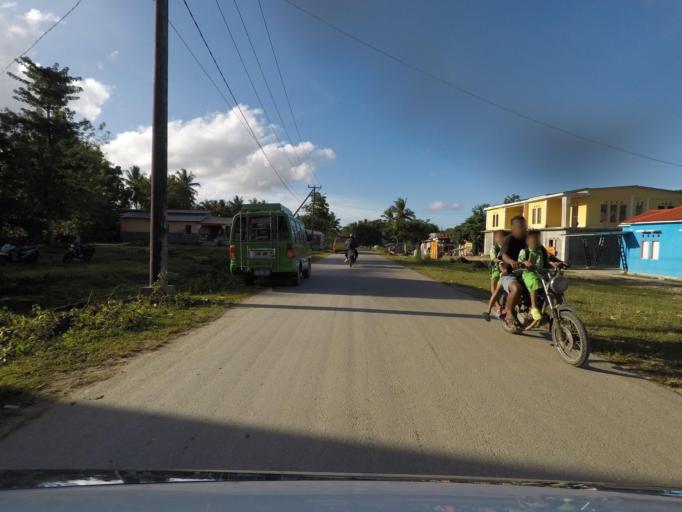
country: TL
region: Lautem
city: Lospalos
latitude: -8.4431
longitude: 127.0058
